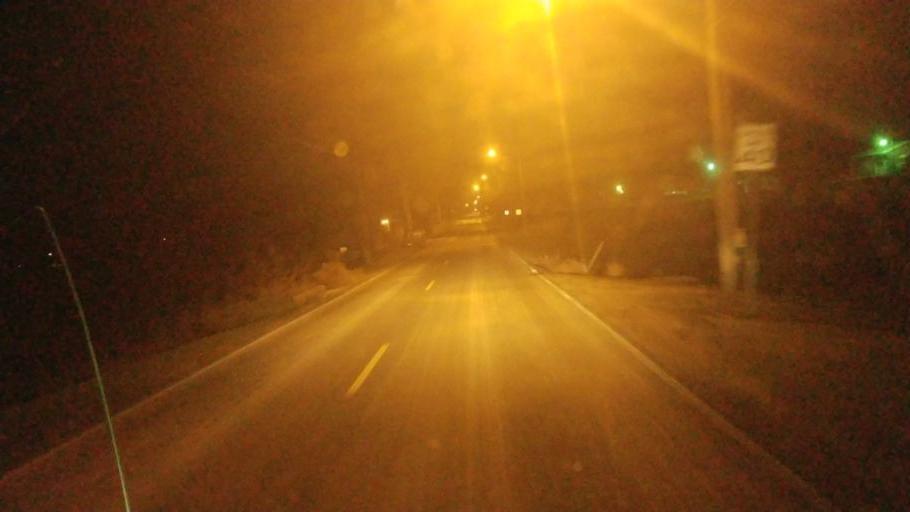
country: US
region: Indiana
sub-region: Adams County
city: Geneva
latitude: 40.5919
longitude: -84.9650
